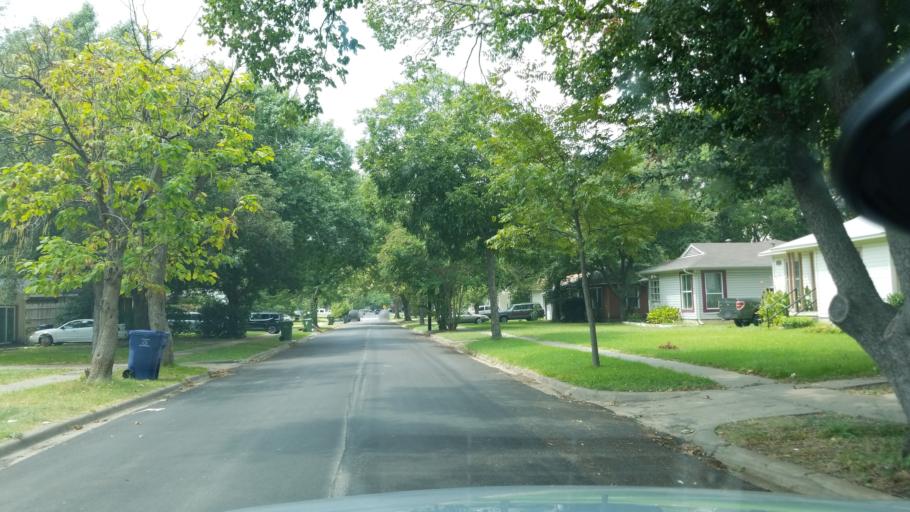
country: US
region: Texas
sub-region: Dallas County
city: Garland
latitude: 32.9218
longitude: -96.6501
